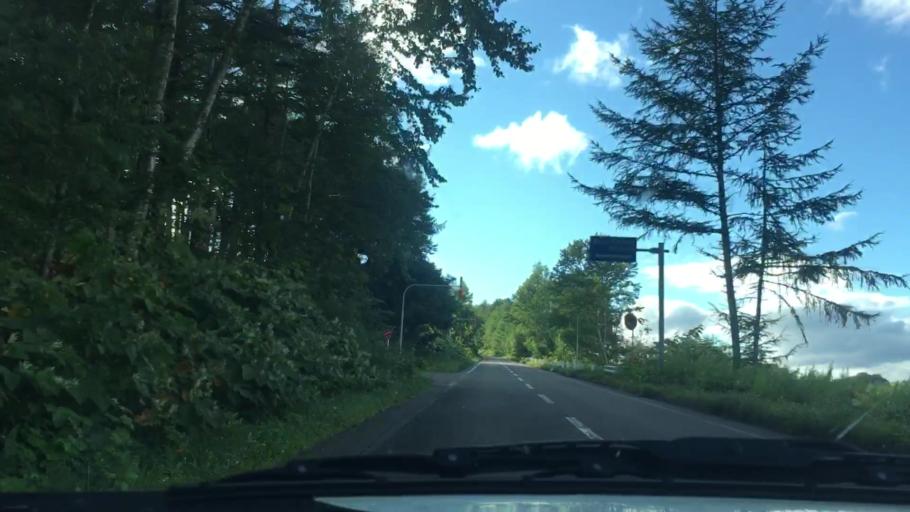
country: JP
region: Hokkaido
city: Otofuke
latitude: 43.1713
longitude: 142.9758
